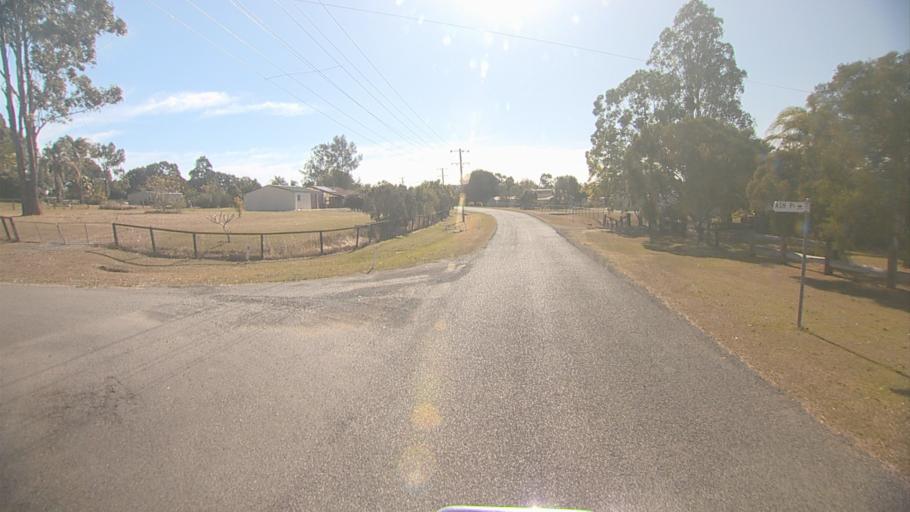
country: AU
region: Queensland
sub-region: Logan
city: Cedar Vale
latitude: -27.8569
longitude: 152.9762
